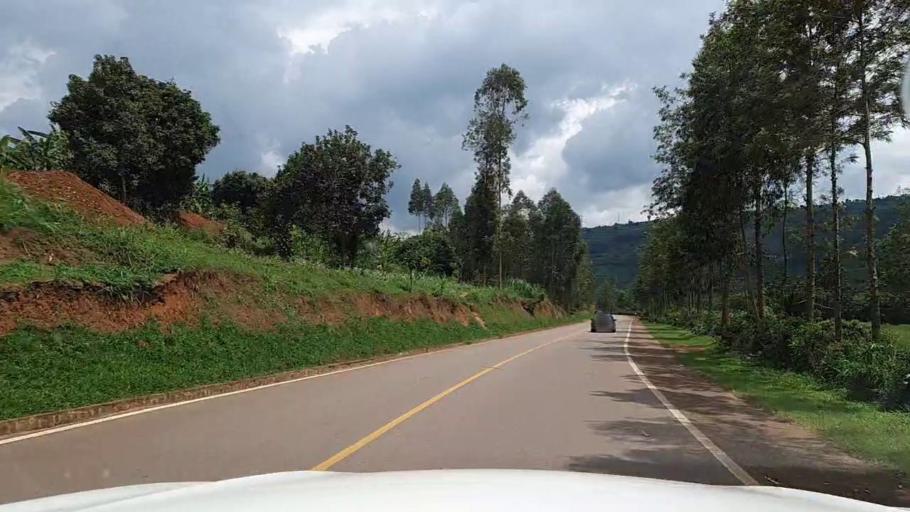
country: RW
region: Kigali
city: Kigali
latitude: -1.8043
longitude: 30.1262
